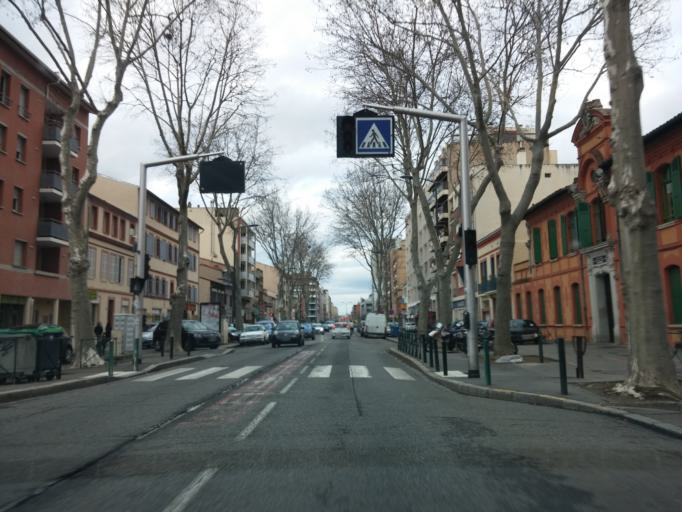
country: FR
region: Midi-Pyrenees
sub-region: Departement de la Haute-Garonne
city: Toulouse
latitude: 43.5824
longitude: 1.4486
